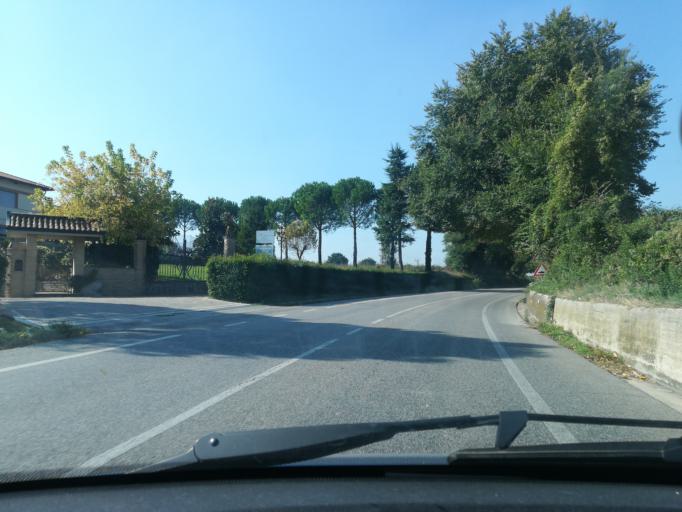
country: IT
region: The Marches
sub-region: Provincia di Macerata
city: Zona Industriale
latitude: 43.2649
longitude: 13.4567
